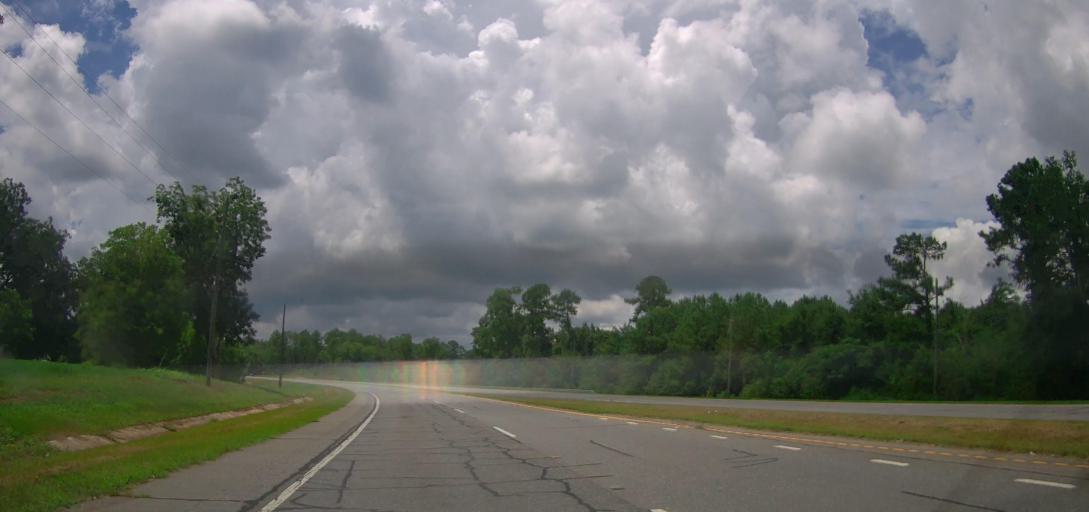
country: US
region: Georgia
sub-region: Pulaski County
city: Hawkinsville
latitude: 32.2603
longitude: -83.4006
